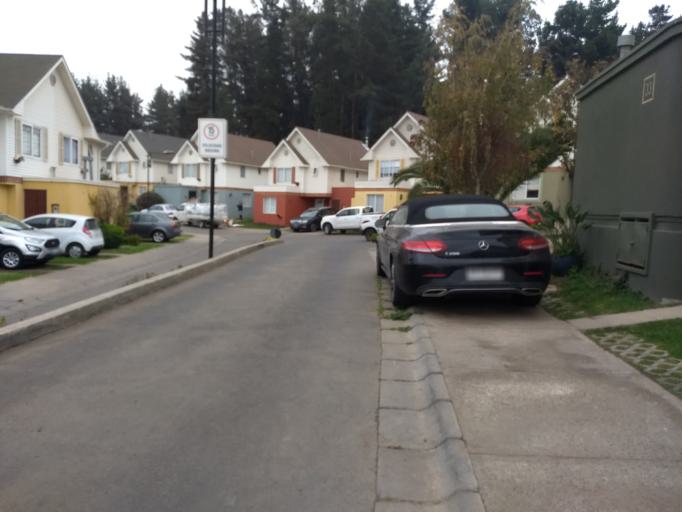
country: CL
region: Valparaiso
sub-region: Provincia de Valparaiso
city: Vina del Mar
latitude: -32.9638
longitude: -71.5189
